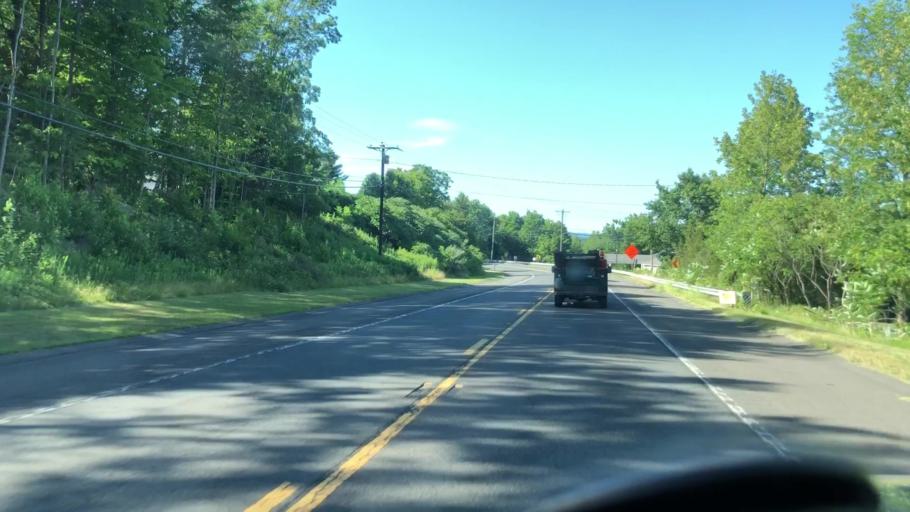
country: US
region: Massachusetts
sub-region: Hampshire County
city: Southampton
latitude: 42.2081
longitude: -72.7258
